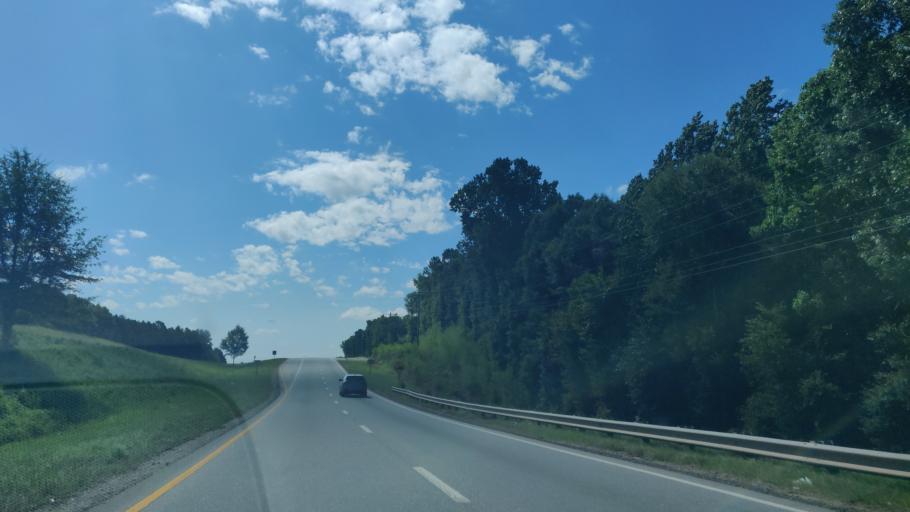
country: US
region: Alabama
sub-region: Lee County
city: Opelika
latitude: 32.6203
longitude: -85.2721
